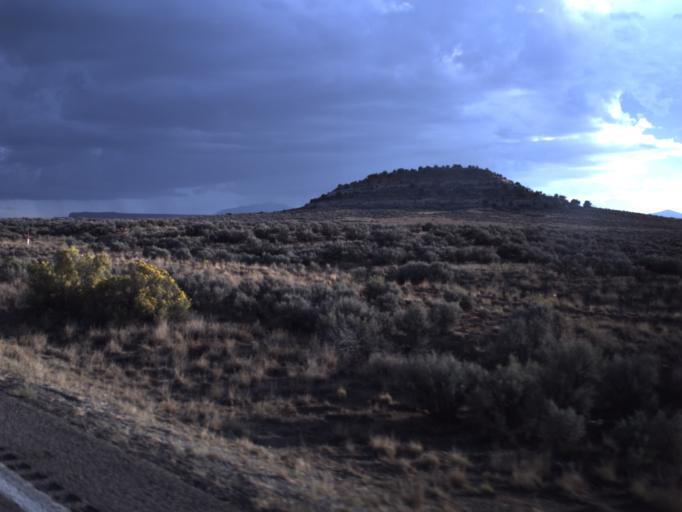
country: US
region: Utah
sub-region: San Juan County
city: Monticello
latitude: 38.1069
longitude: -109.3631
